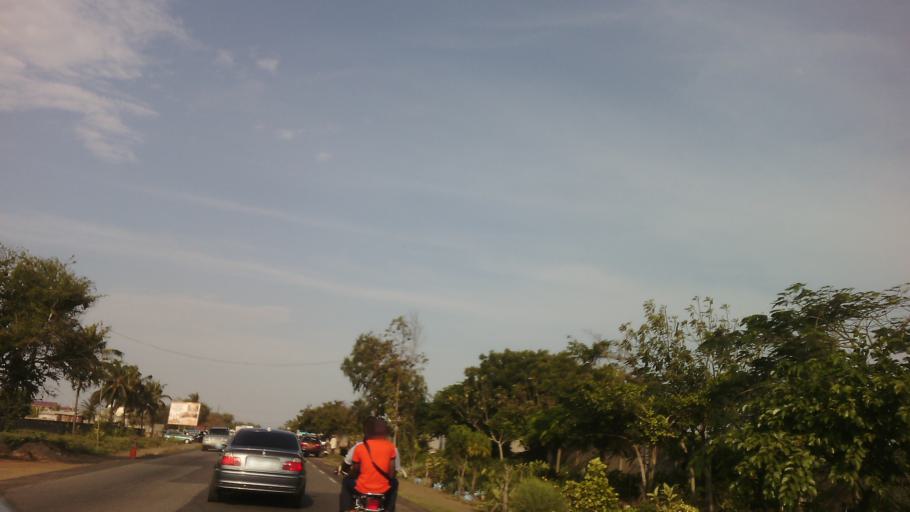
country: TG
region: Maritime
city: Lome
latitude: 6.1774
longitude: 1.3725
